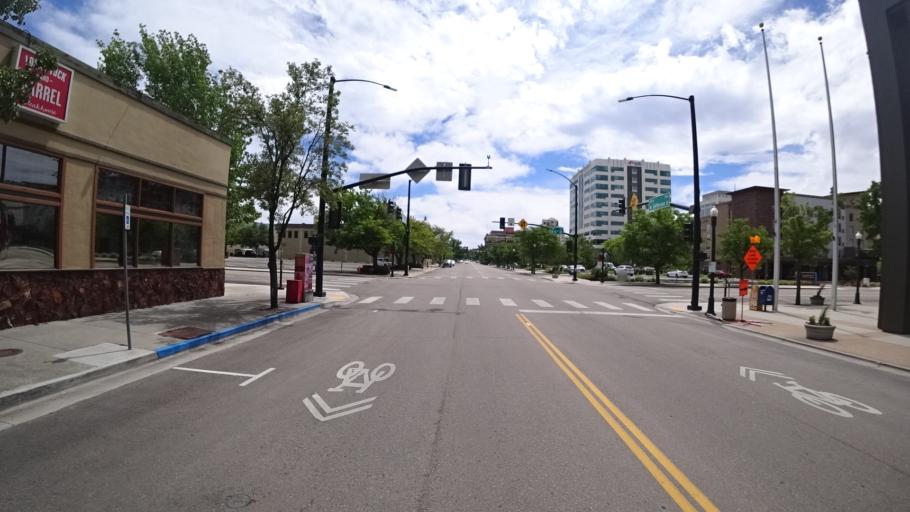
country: US
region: Idaho
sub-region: Ada County
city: Boise
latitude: 43.6198
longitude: -116.2049
